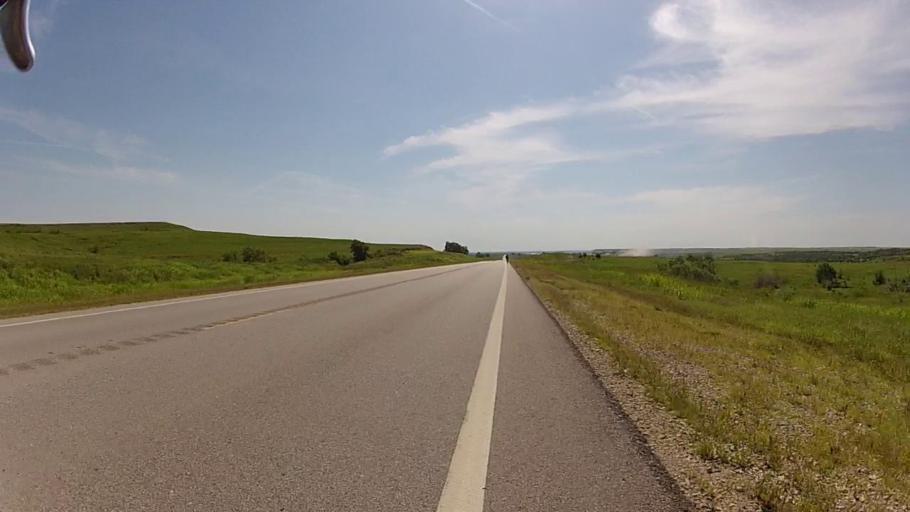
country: US
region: Kansas
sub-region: Cowley County
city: Winfield
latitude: 37.1107
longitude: -96.6352
